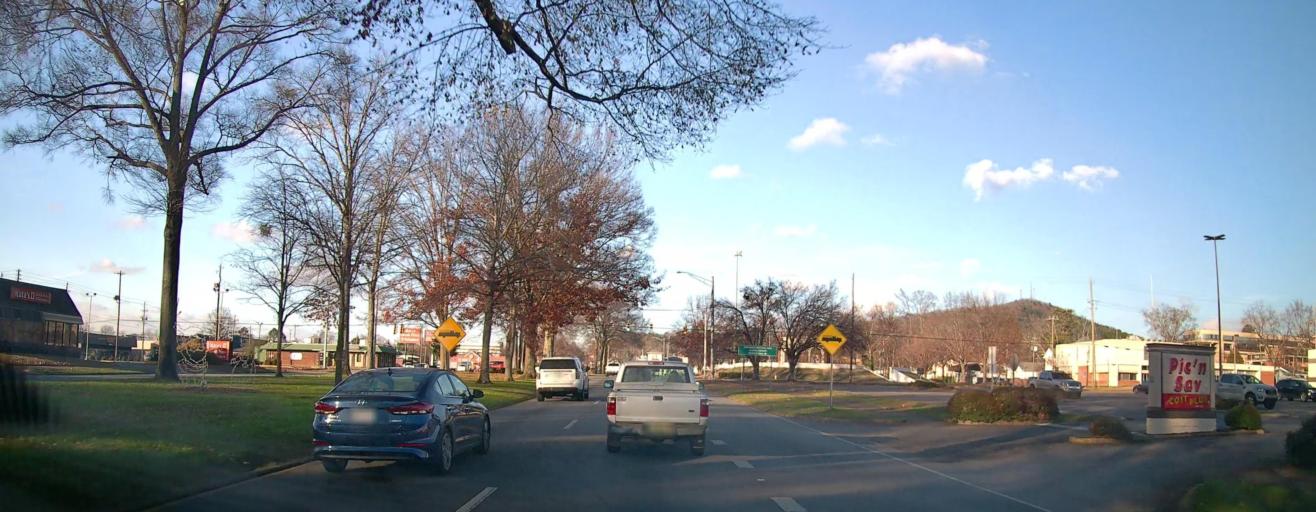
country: US
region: Alabama
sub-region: Calhoun County
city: Anniston
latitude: 33.6655
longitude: -85.8266
